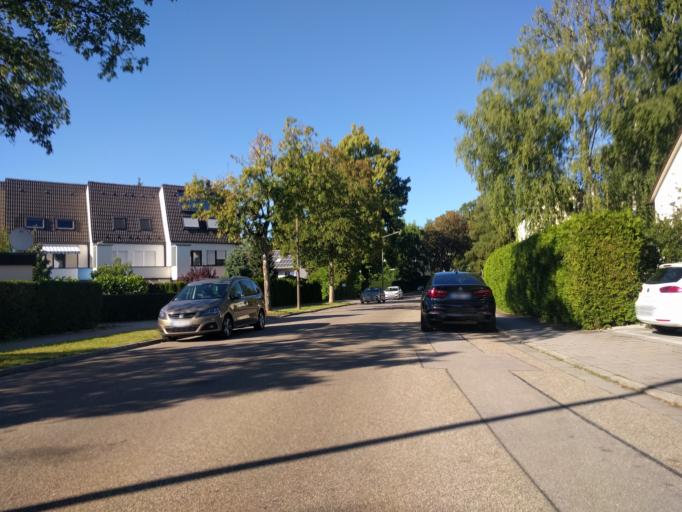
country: DE
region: Bavaria
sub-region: Upper Palatinate
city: Pentling
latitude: 49.0071
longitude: 12.0755
